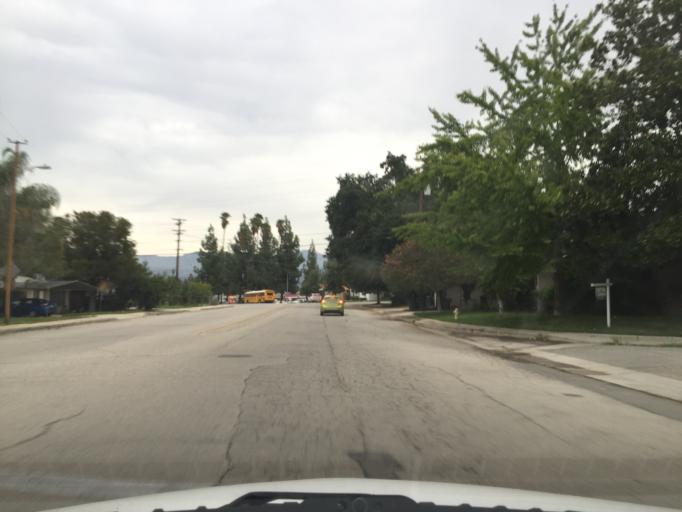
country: US
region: California
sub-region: San Bernardino County
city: Redlands
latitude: 34.0559
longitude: -117.1922
